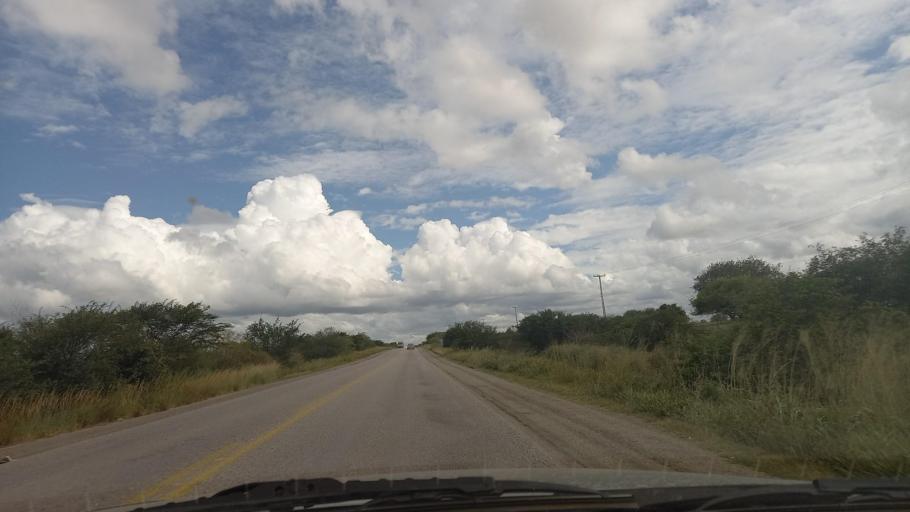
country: BR
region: Pernambuco
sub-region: Cachoeirinha
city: Cachoeirinha
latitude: -8.4327
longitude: -36.2010
